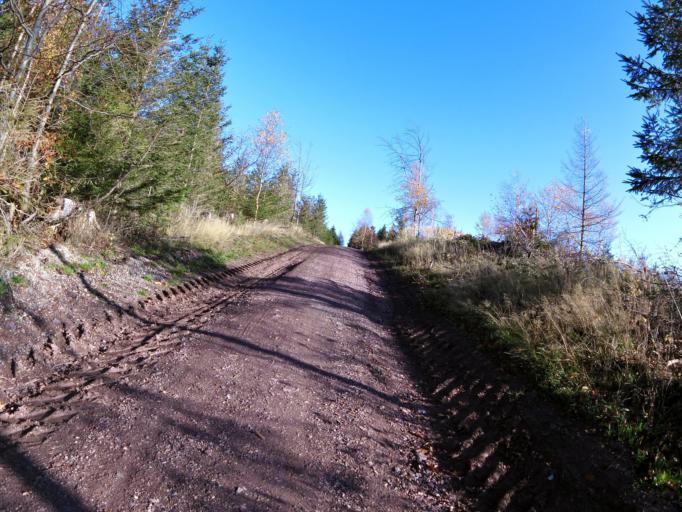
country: DE
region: Thuringia
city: Ruhla
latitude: 50.9058
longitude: 10.3505
